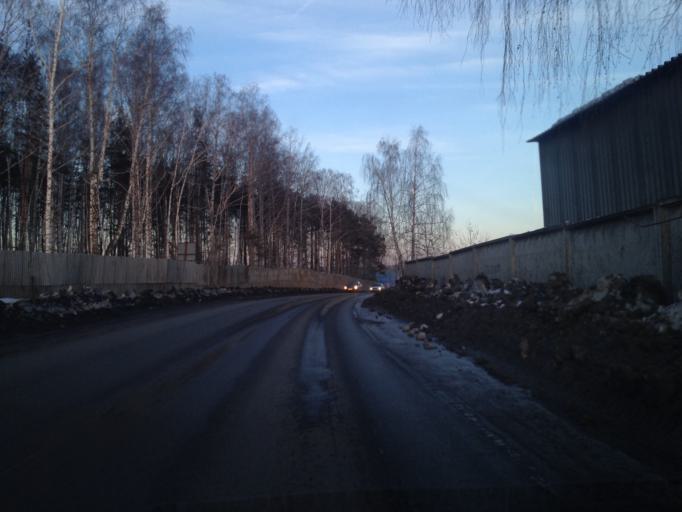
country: RU
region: Sverdlovsk
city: Istok
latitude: 56.7614
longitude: 60.7336
